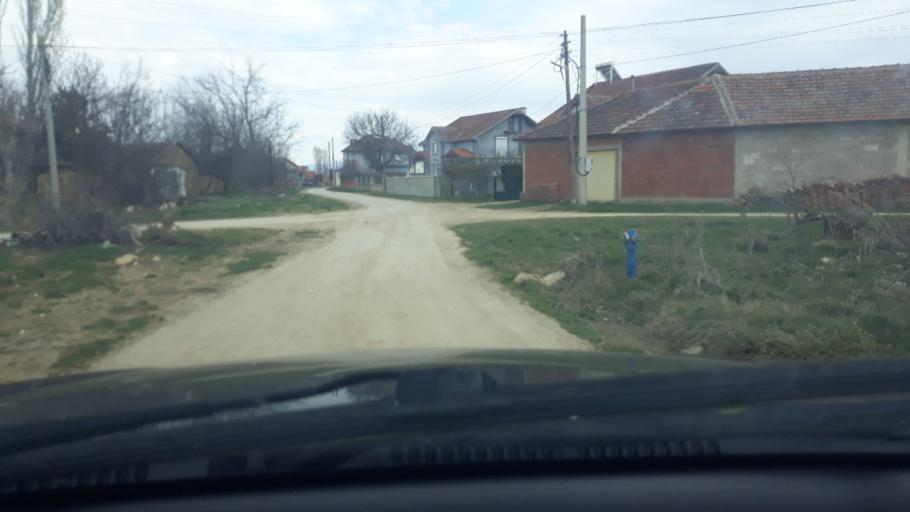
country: MK
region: Krusevo
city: Bucin
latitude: 41.2797
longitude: 21.3374
